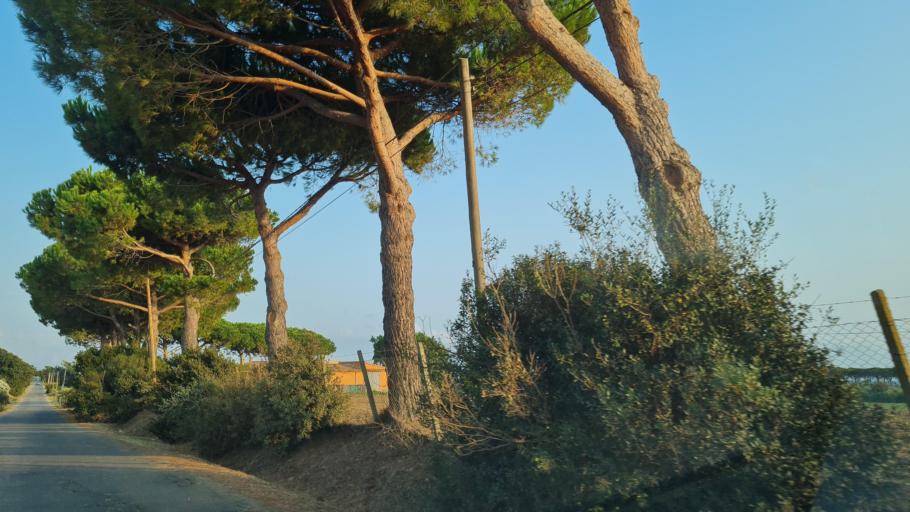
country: IT
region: Latium
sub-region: Provincia di Viterbo
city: Montalto di Castro
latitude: 42.3105
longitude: 11.6183
